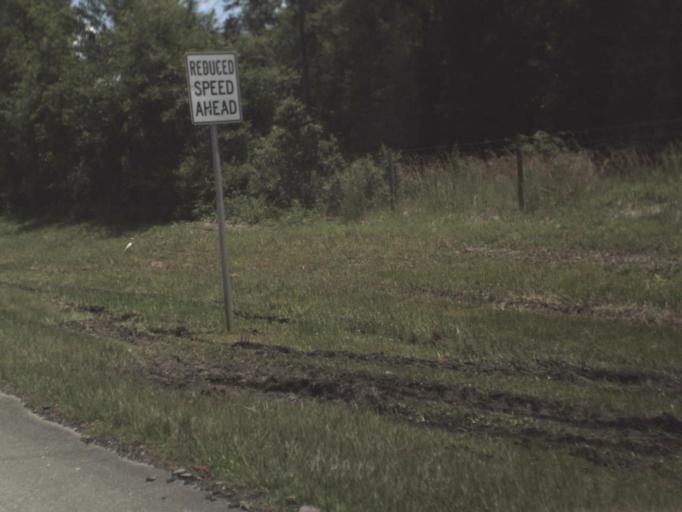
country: US
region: Florida
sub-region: Union County
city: Lake Butler
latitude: 29.9174
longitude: -82.4271
